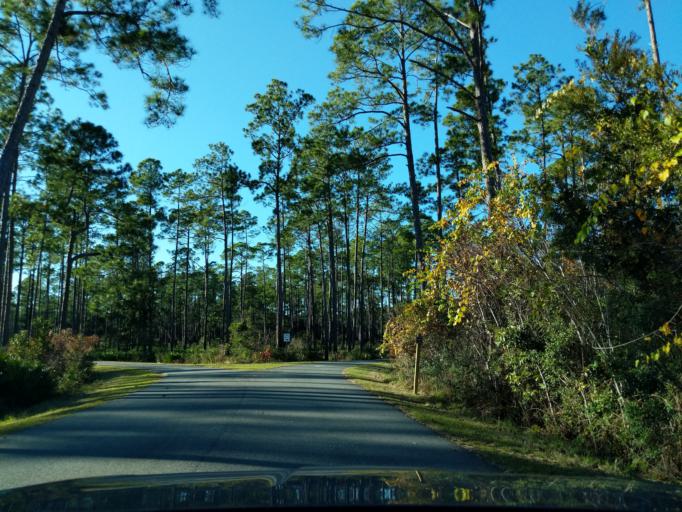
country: US
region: Georgia
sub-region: Charlton County
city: Folkston
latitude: 30.7117
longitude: -82.1538
